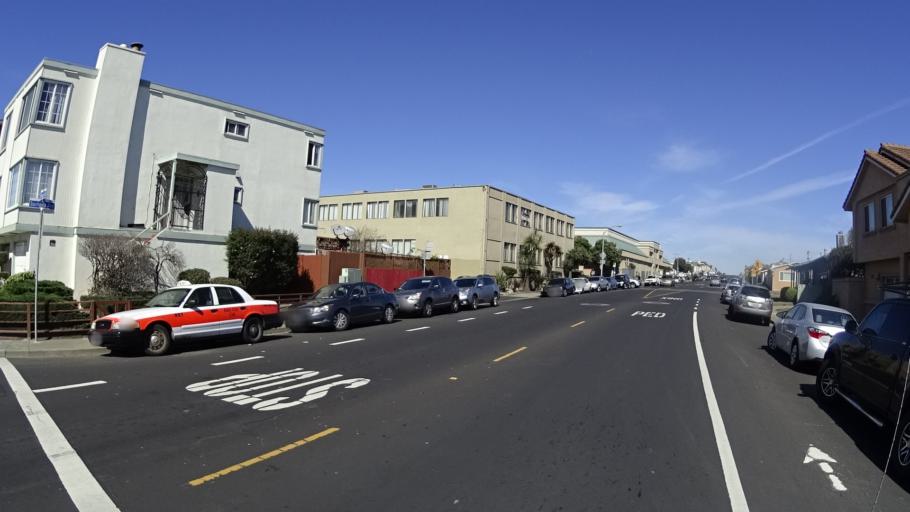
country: US
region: California
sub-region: San Mateo County
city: Broadmoor
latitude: 37.6811
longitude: -122.4870
